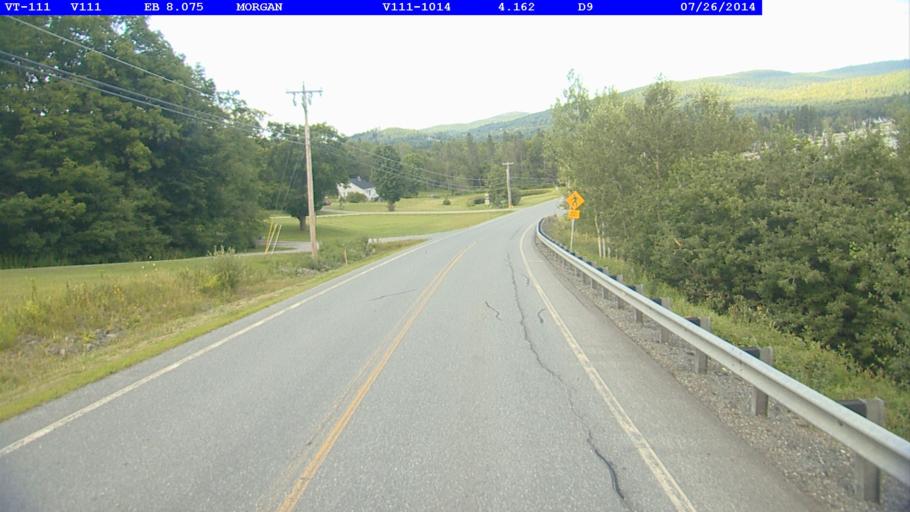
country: US
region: Vermont
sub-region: Orleans County
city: Newport
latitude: 44.9095
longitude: -71.9918
